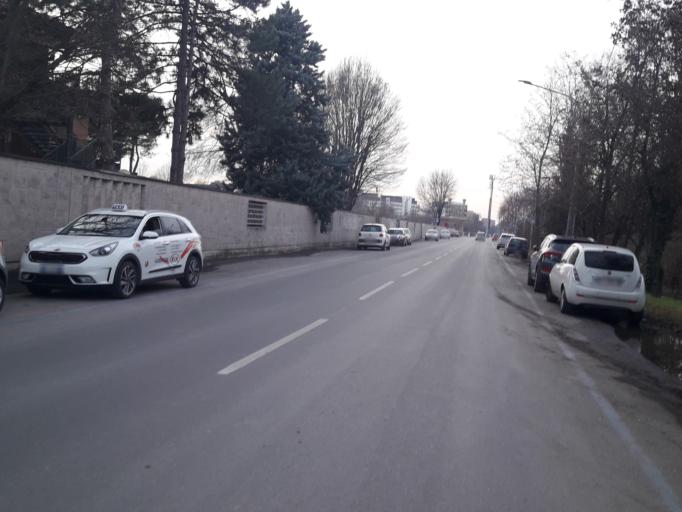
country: IT
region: Emilia-Romagna
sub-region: Provincia di Bologna
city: Bologna
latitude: 44.5069
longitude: 11.3144
